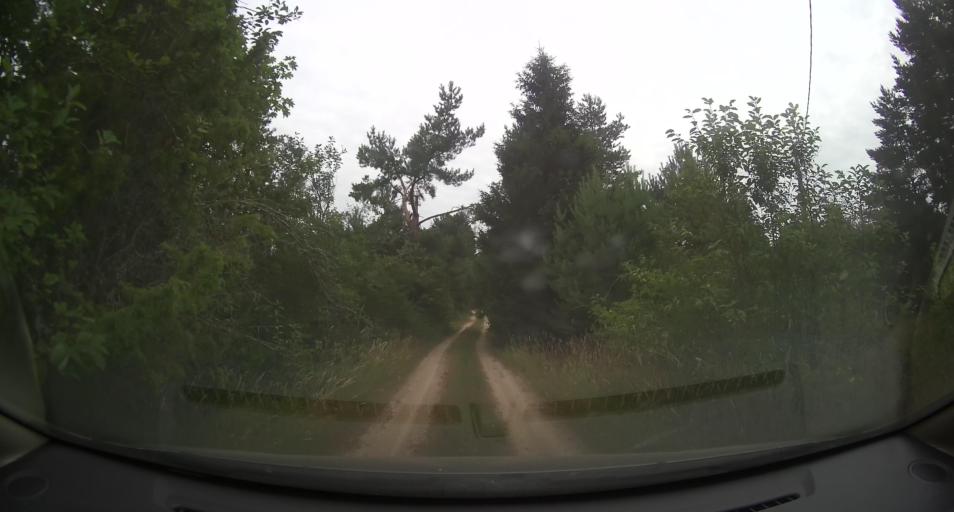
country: EE
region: Laeaene
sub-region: Lihula vald
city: Lihula
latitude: 58.5920
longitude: 23.7258
